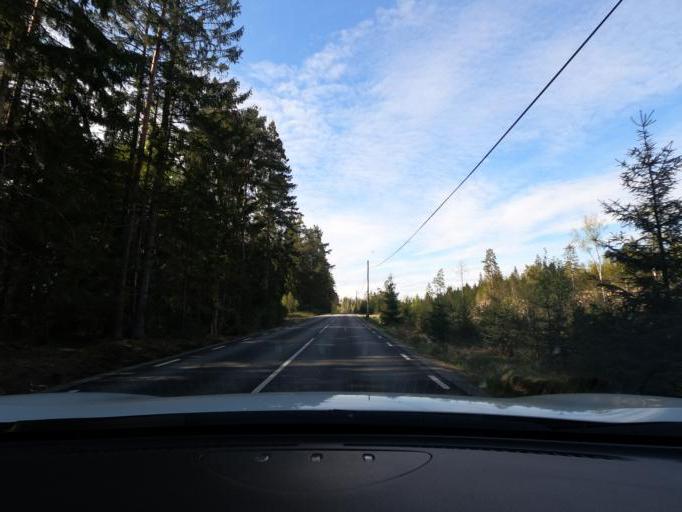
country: SE
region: Vaestra Goetaland
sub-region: Harryda Kommun
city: Landvetter
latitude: 57.6541
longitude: 12.2627
